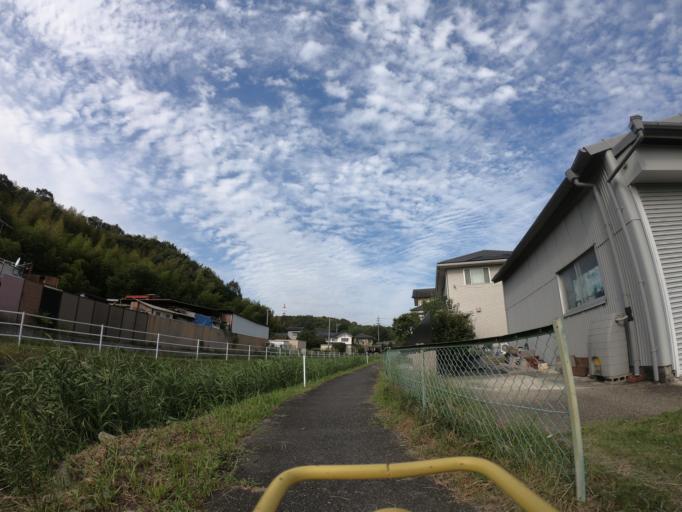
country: JP
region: Aichi
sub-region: Toyota-shi
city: Toyota
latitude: 35.1406
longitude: 137.0785
